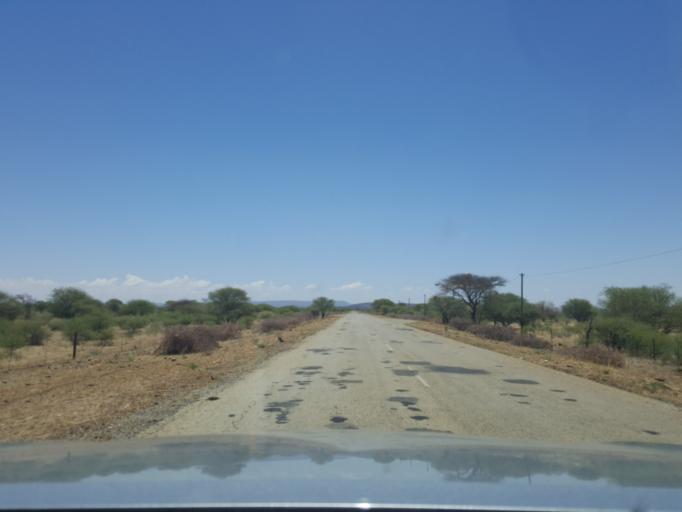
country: BW
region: South East
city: Ramotswa
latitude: -25.0325
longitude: 25.9255
